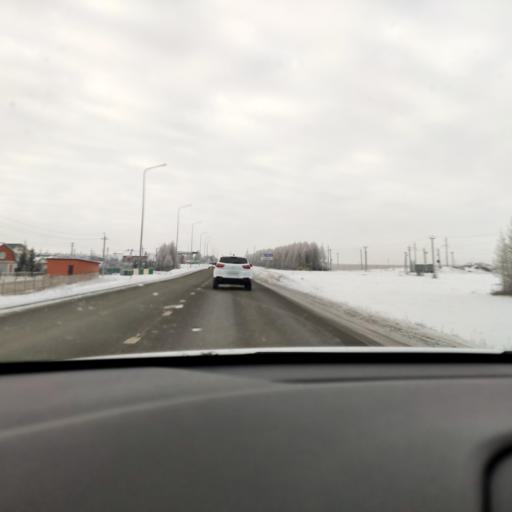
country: RU
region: Tatarstan
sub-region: Arskiy Rayon
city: Arsk
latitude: 56.1061
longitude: 49.8903
